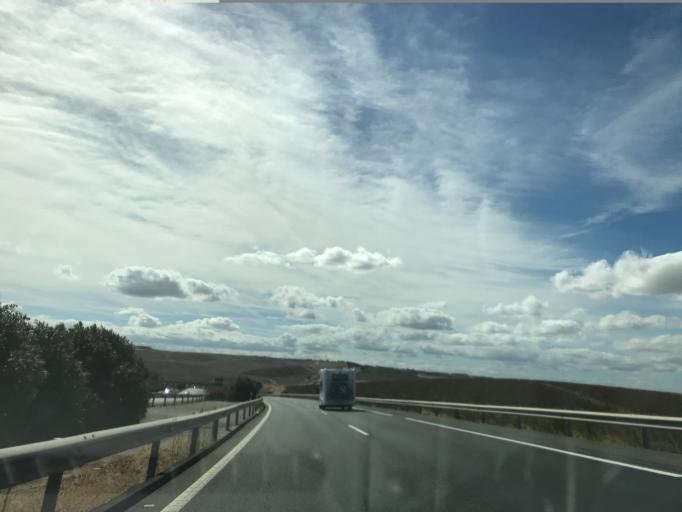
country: ES
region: Andalusia
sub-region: Province of Cordoba
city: La Victoria
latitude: 37.7436
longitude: -4.8491
